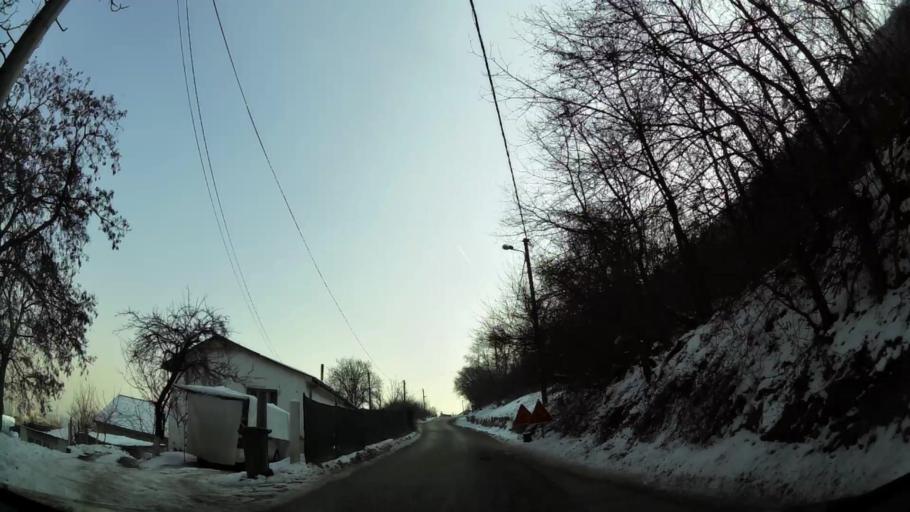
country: MK
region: Sopiste
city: Sopishte
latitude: 41.9722
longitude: 21.4354
